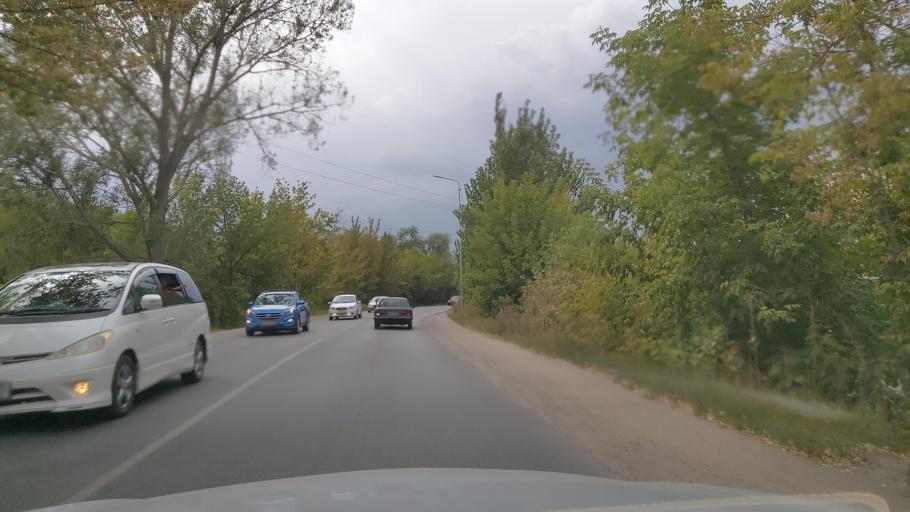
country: KZ
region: Almaty Oblysy
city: Energeticheskiy
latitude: 43.4034
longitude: 77.0275
